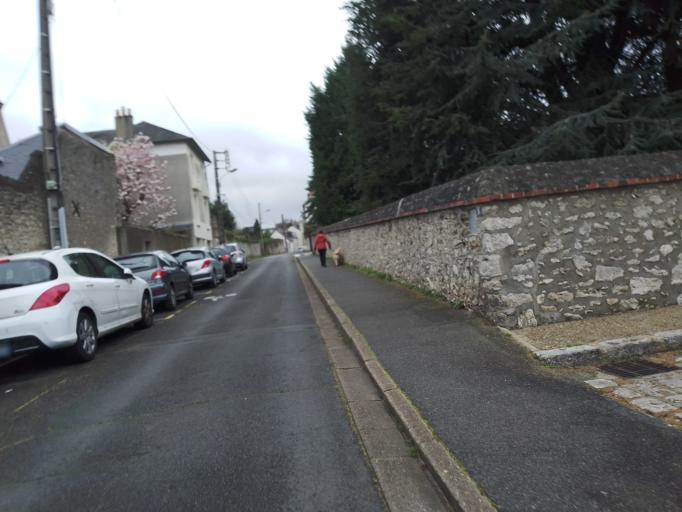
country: FR
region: Centre
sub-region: Departement du Loir-et-Cher
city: Blois
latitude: 47.5914
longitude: 1.3393
